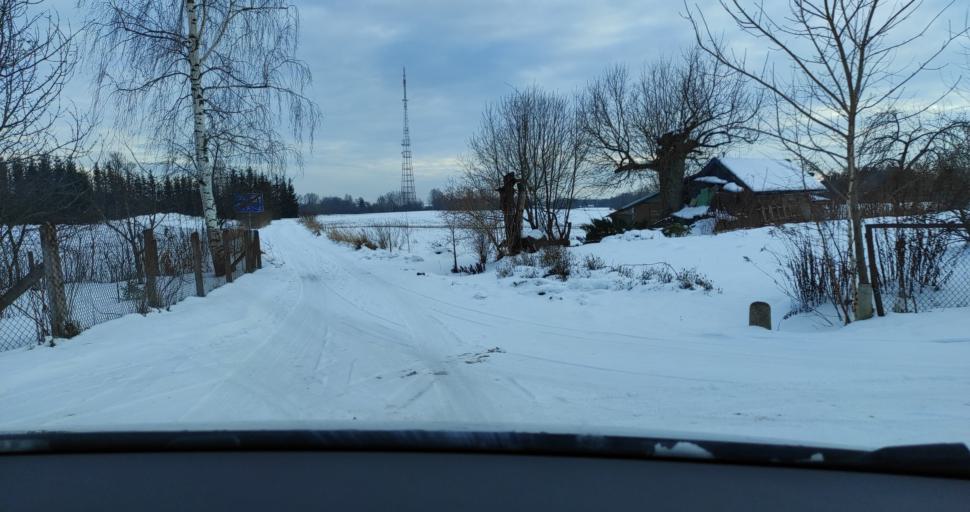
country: LV
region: Kuldigas Rajons
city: Kuldiga
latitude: 56.9428
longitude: 22.0060
